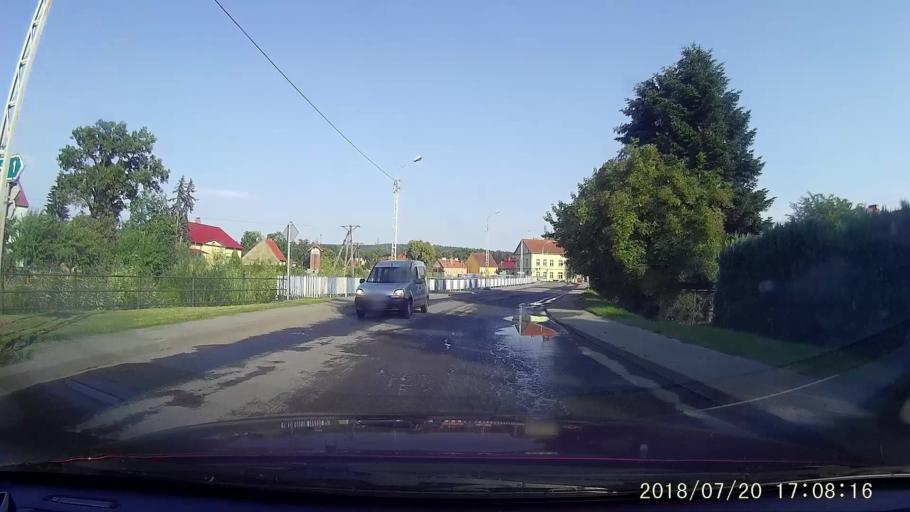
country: PL
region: Lower Silesian Voivodeship
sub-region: Powiat lubanski
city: Lesna
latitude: 51.0249
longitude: 15.2625
